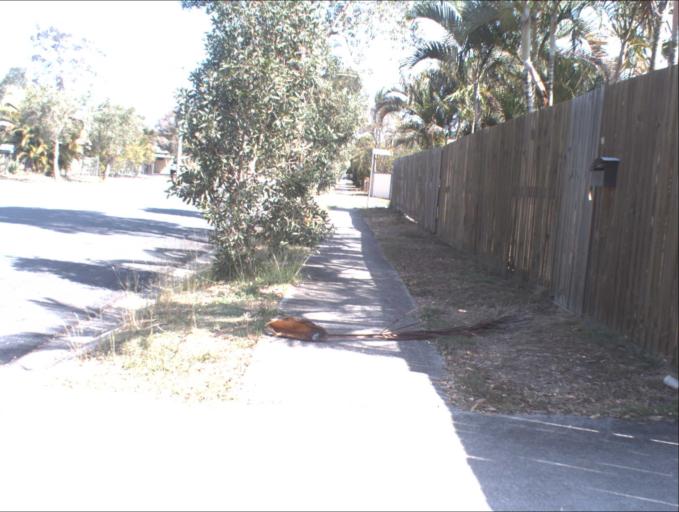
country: AU
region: Queensland
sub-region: Logan
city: Beenleigh
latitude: -27.6888
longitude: 153.1884
